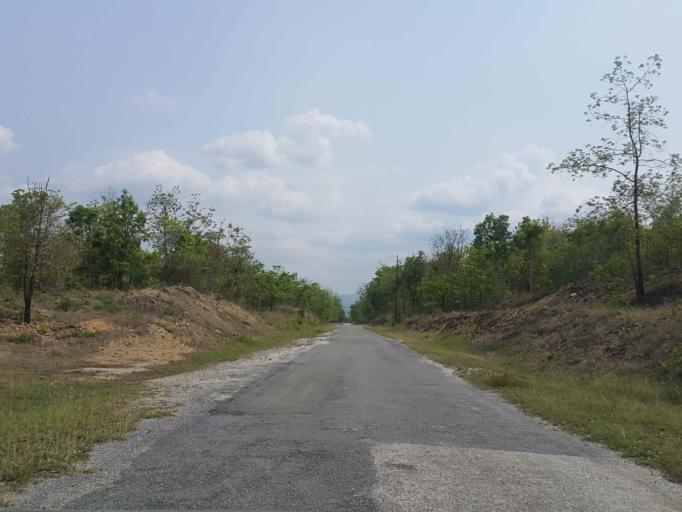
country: TH
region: Sukhothai
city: Thung Saliam
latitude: 17.3336
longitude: 99.4239
